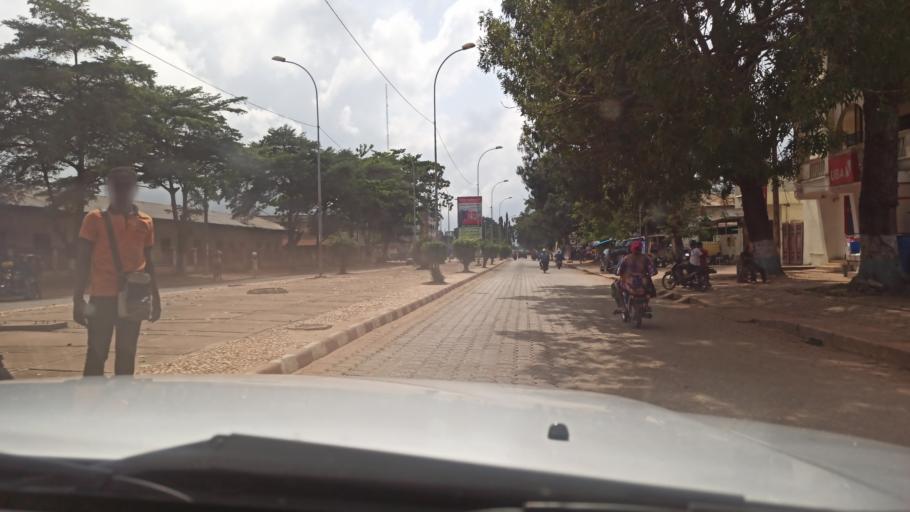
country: BJ
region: Queme
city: Porto-Novo
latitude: 6.4807
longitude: 2.6321
